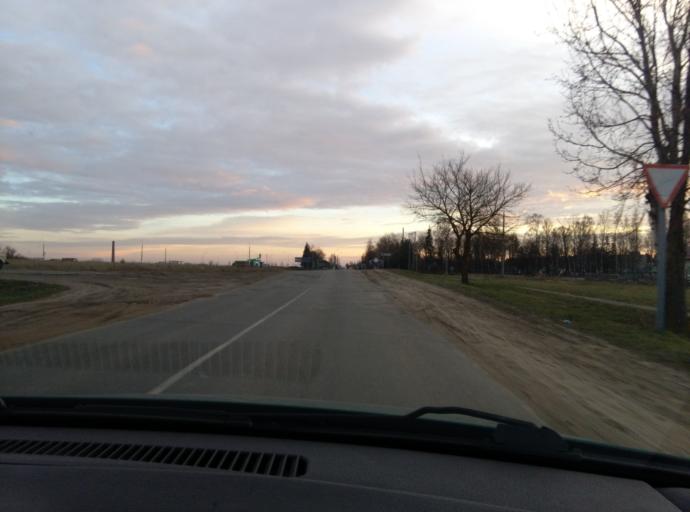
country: BY
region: Minsk
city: Horad Barysaw
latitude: 54.2748
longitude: 28.4963
